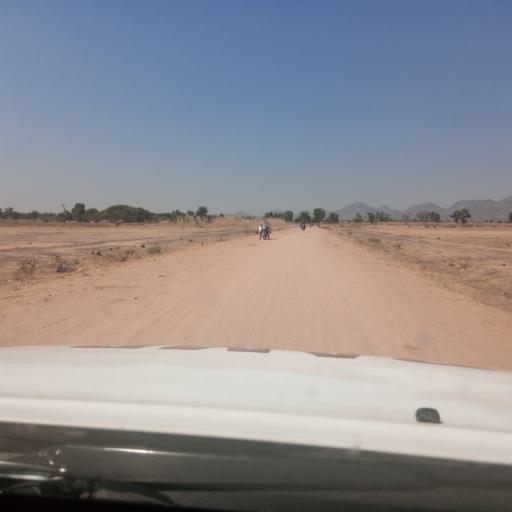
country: NG
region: Adamawa
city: Little Gombi
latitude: 9.7757
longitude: 12.5870
